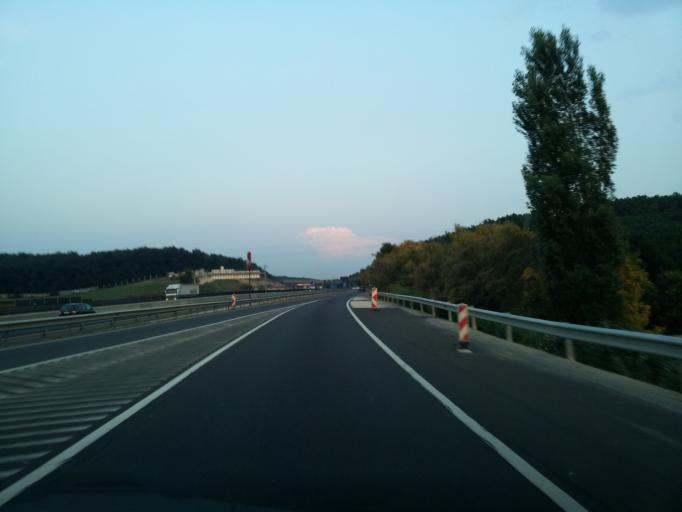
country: HU
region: Pest
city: Toeroekbalint
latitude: 47.4282
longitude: 18.8978
